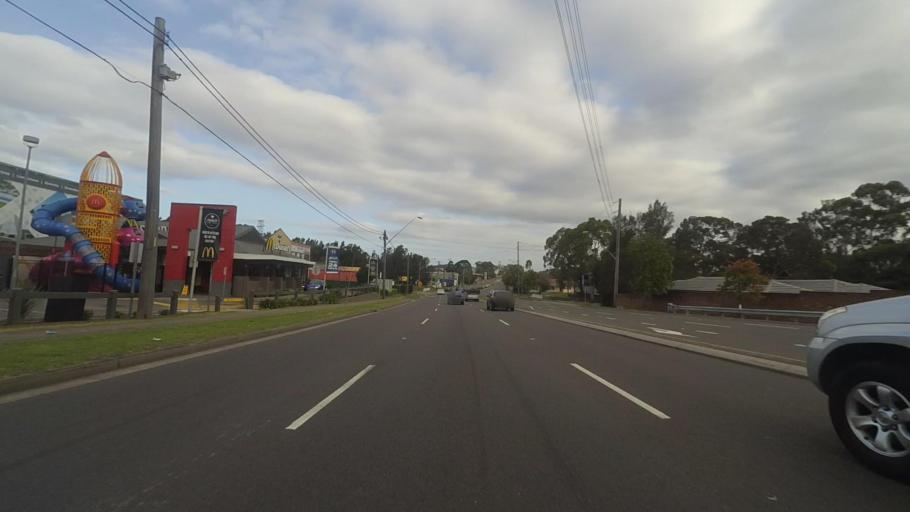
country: AU
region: New South Wales
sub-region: Bankstown
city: Padstow
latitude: -33.9458
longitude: 151.0353
